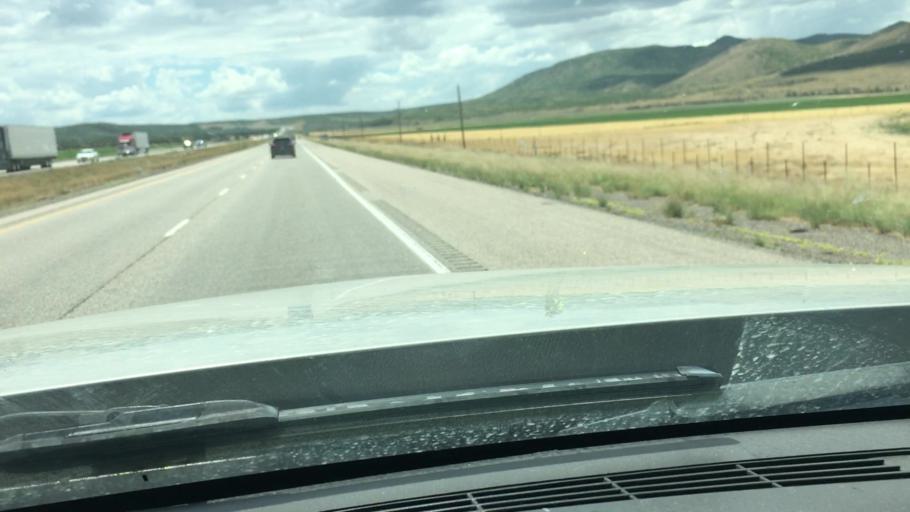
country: US
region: Utah
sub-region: Beaver County
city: Beaver
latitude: 38.5252
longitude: -112.6119
